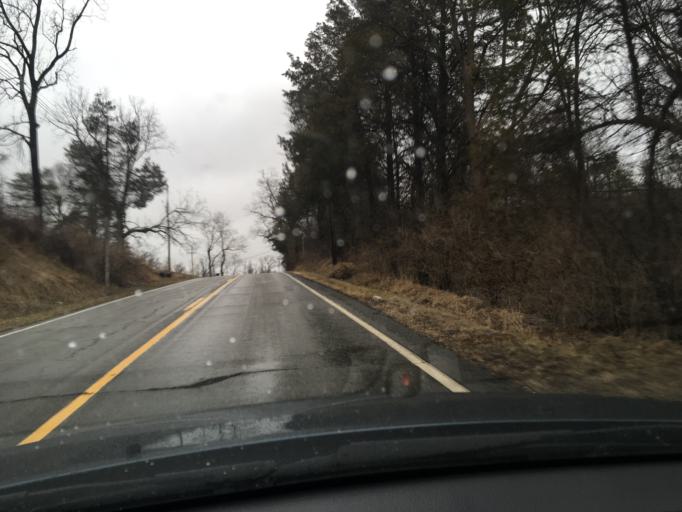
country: US
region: Michigan
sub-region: Jackson County
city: Grass Lake
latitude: 42.3371
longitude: -84.1523
